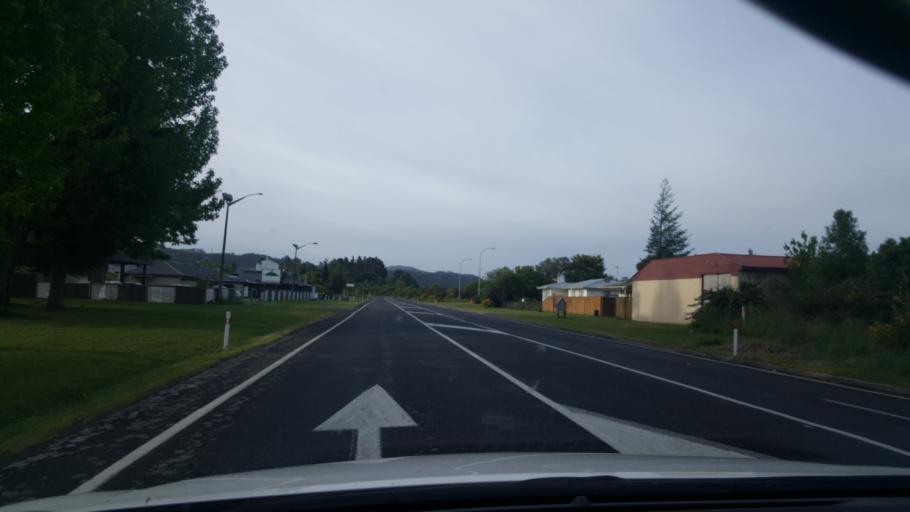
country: NZ
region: Waikato
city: Turangi
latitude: -38.9646
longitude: 175.7663
